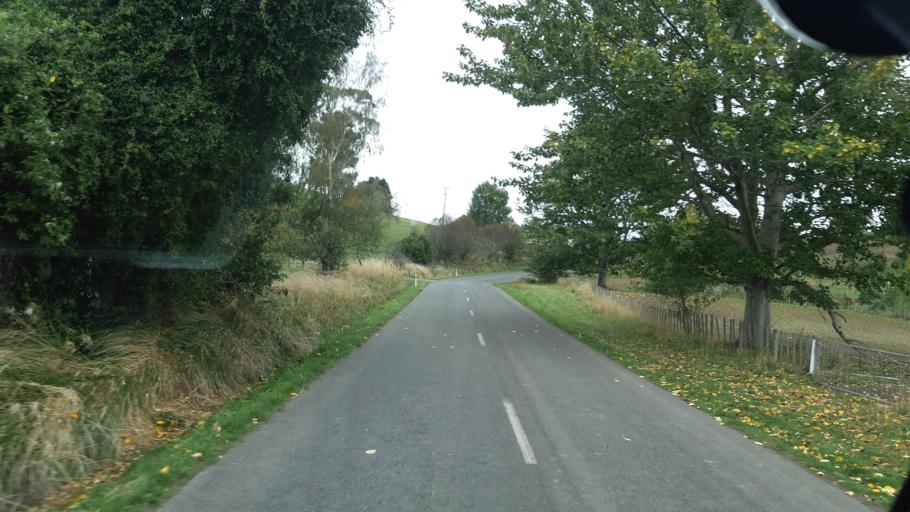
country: NZ
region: Manawatu-Wanganui
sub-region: Ruapehu District
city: Waiouru
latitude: -39.5570
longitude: 175.6245
